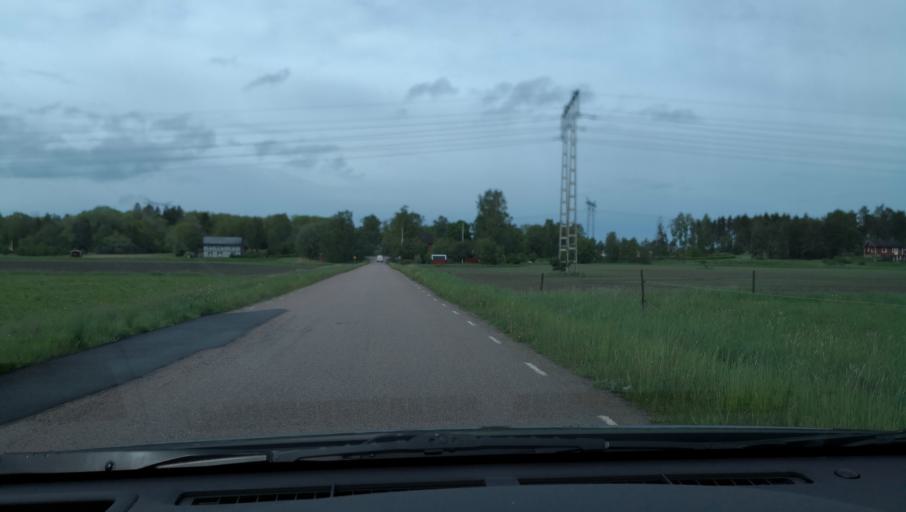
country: SE
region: Uppsala
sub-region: Enkopings Kommun
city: Orsundsbro
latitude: 59.6860
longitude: 17.3796
